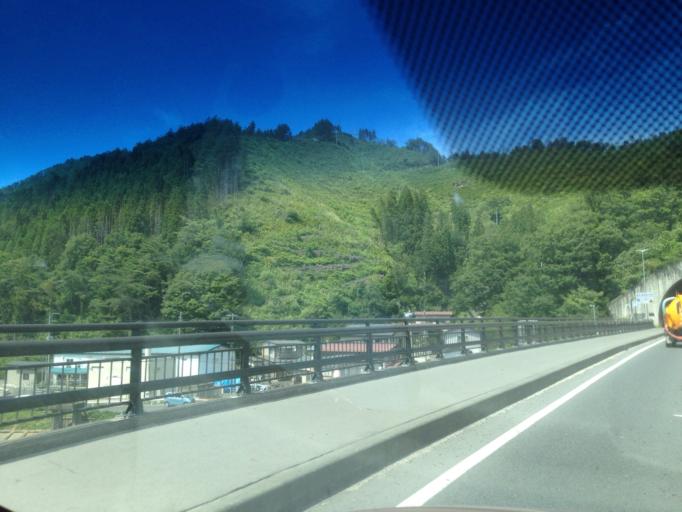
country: JP
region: Iwate
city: Otsuchi
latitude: 39.3568
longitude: 141.8933
